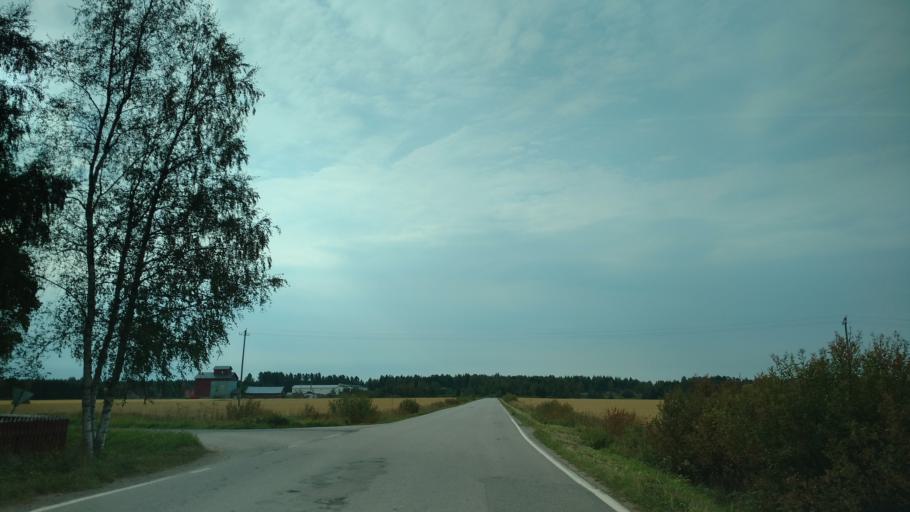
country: FI
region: Varsinais-Suomi
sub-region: Loimaa
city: Koski Tl
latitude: 60.6923
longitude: 23.1636
